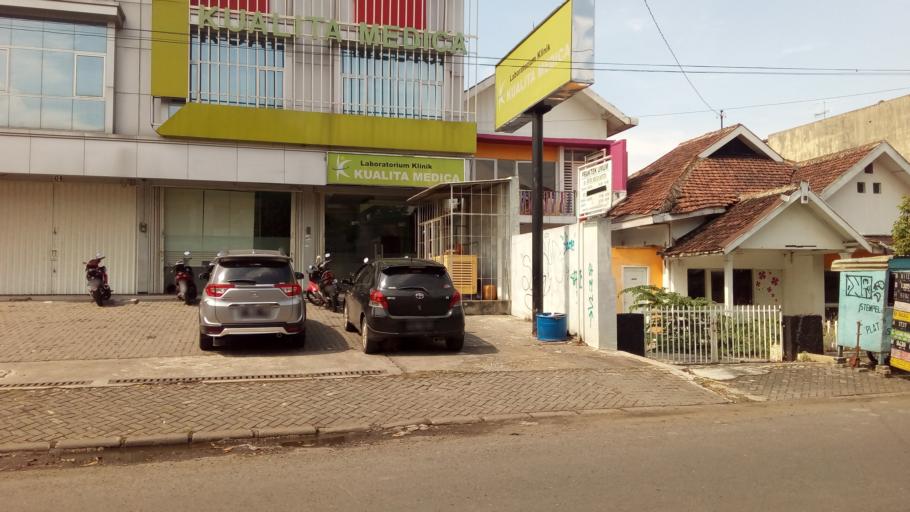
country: ID
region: Central Java
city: Semarang
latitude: -7.0057
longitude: 110.4366
